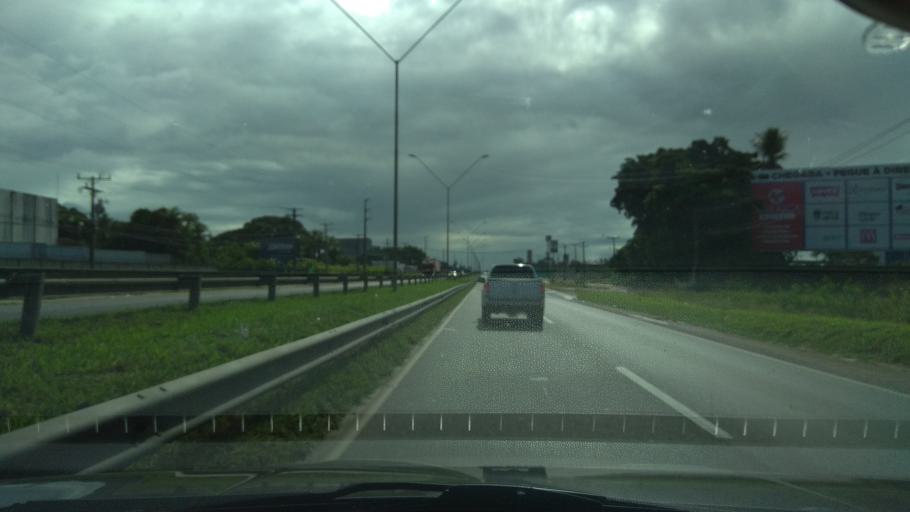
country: BR
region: Bahia
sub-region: Feira De Santana
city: Feira de Santana
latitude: -12.3077
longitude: -38.8888
